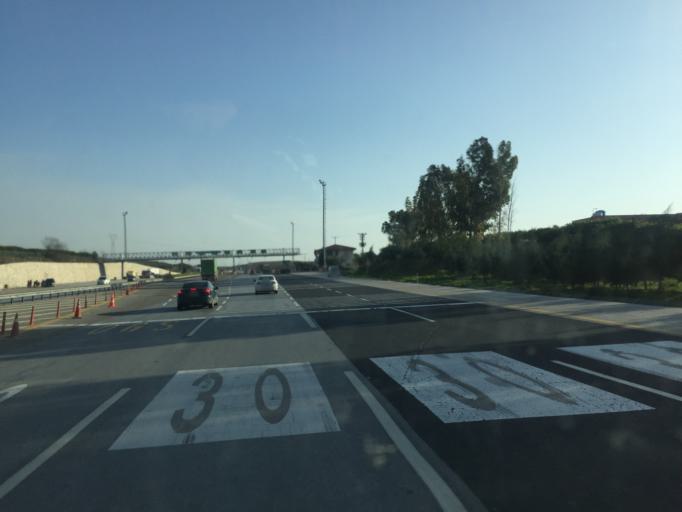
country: TR
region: Mersin
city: Yenice
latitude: 37.0274
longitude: 35.1114
